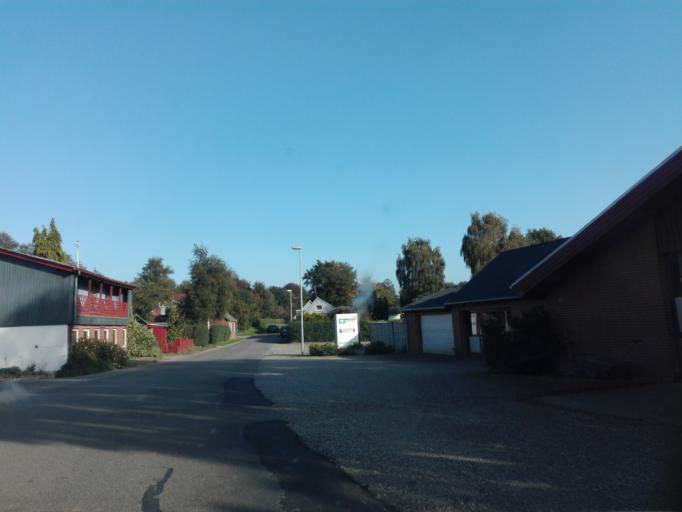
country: DK
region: Central Jutland
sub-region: Odder Kommune
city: Odder
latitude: 55.9290
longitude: 10.1920
